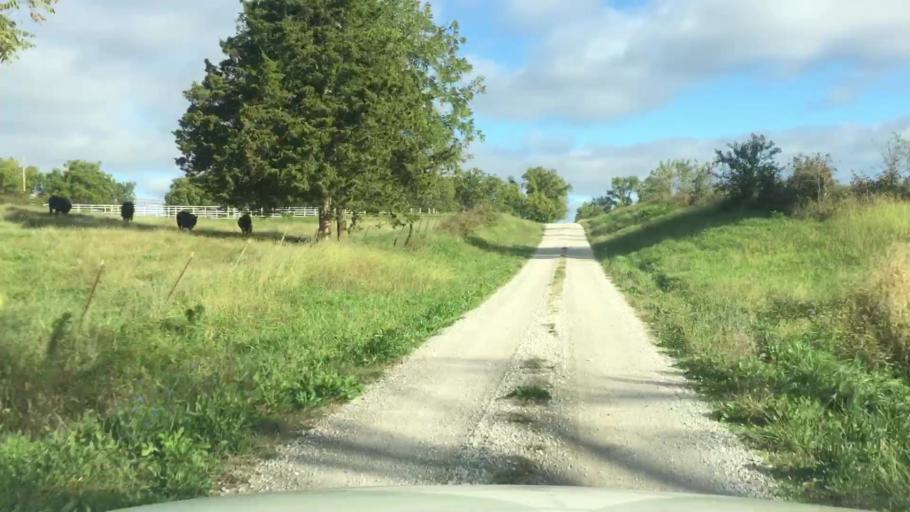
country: US
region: Missouri
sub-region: Howard County
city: New Franklin
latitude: 39.1022
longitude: -92.7793
